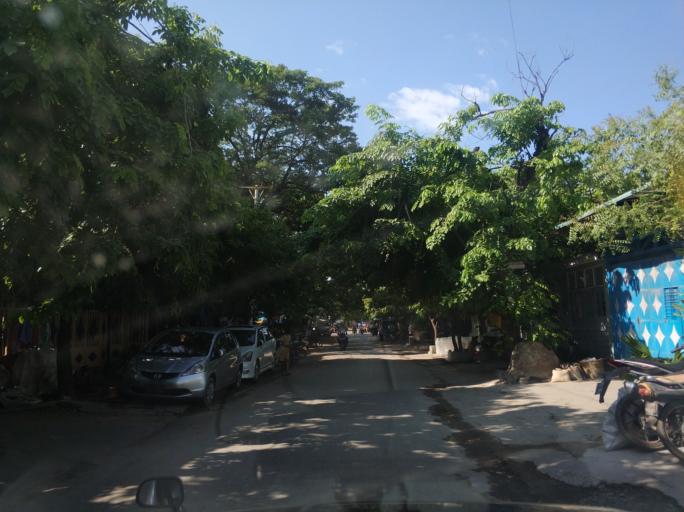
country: MM
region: Mandalay
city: Mandalay
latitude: 21.9709
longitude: 96.0687
